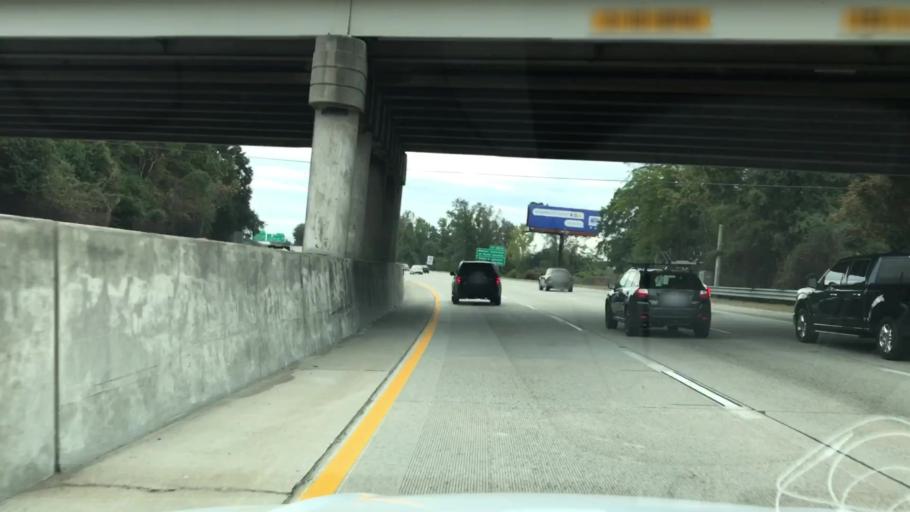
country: US
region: South Carolina
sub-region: Charleston County
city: North Charleston
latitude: 32.8473
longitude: -79.9870
